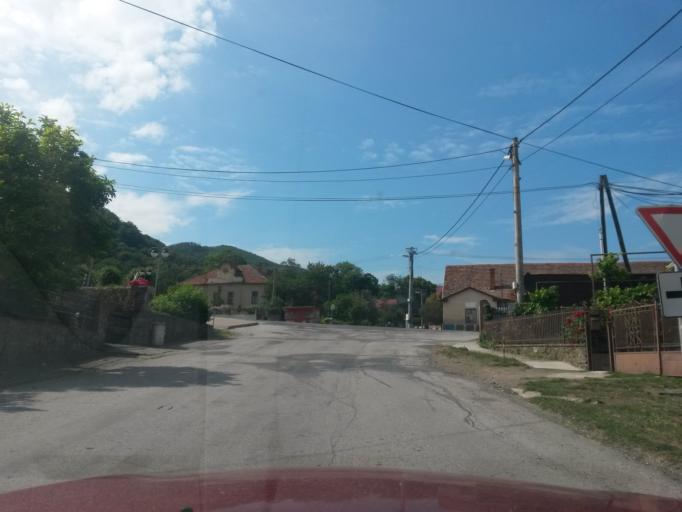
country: SK
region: Kosicky
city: Secovce
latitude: 48.6359
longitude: 21.4787
